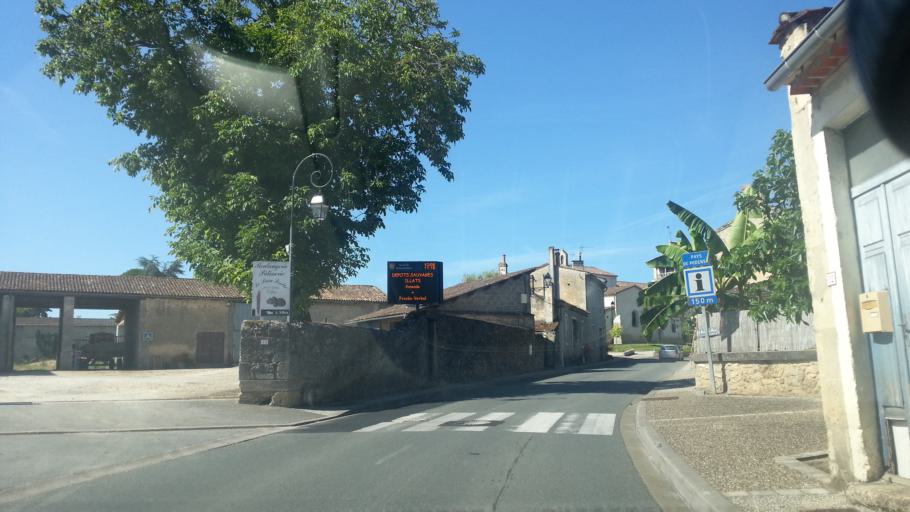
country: FR
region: Aquitaine
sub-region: Departement de la Gironde
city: Illats
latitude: 44.5983
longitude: -0.3712
